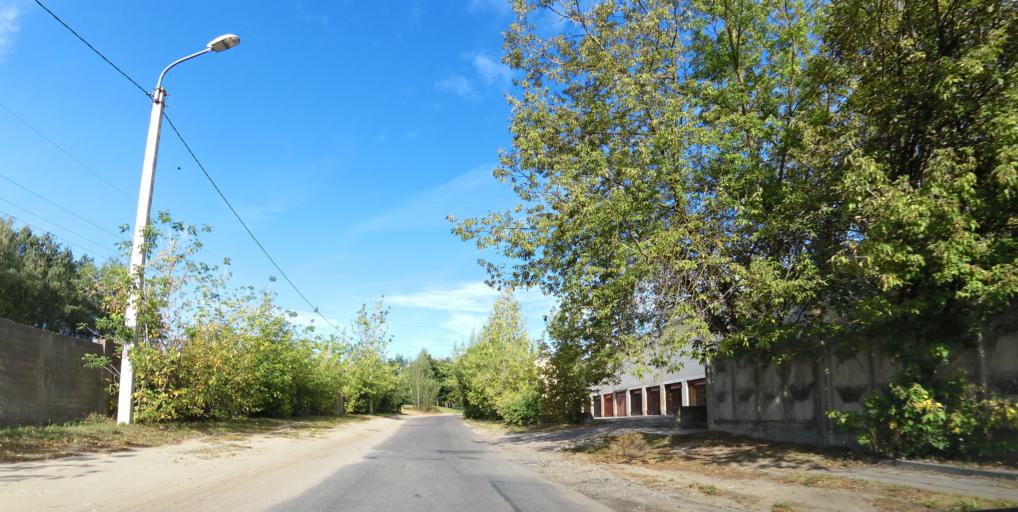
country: LT
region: Vilnius County
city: Seskine
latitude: 54.7133
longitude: 25.2343
